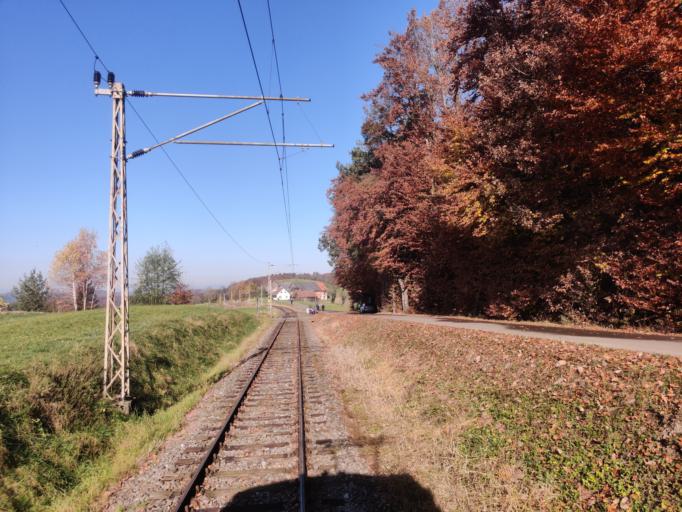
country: AT
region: Styria
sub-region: Politischer Bezirk Suedoststeiermark
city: Maierdorf
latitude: 46.8942
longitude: 15.8344
